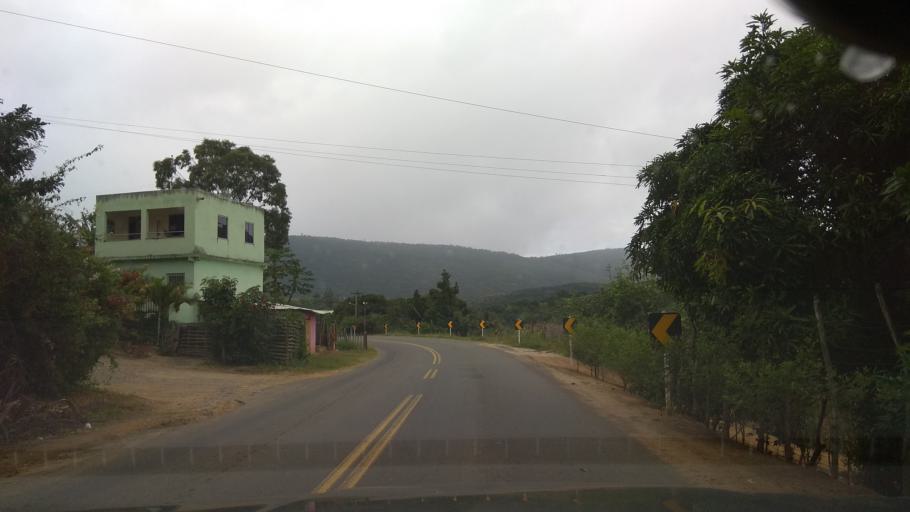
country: BR
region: Bahia
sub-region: Santa Ines
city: Santa Ines
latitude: -13.2420
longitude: -39.7557
